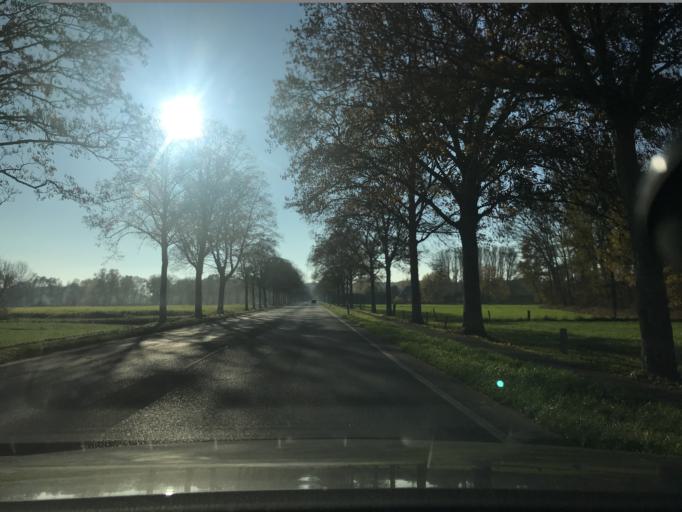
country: DE
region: North Rhine-Westphalia
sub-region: Regierungsbezirk Dusseldorf
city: Wachtendonk
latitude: 51.4252
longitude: 6.3679
